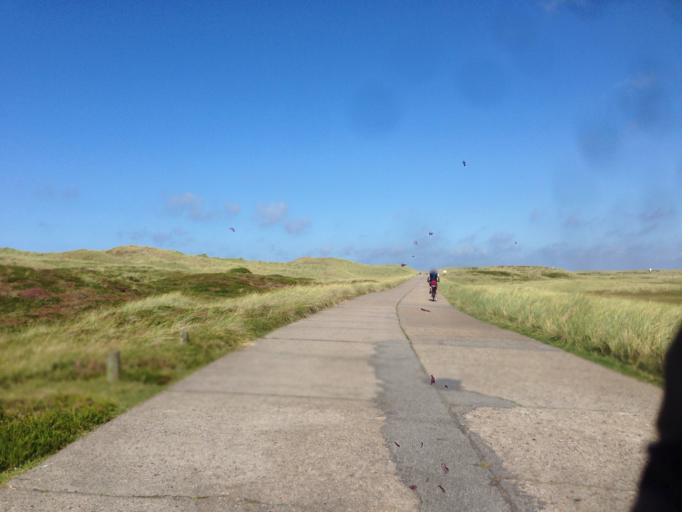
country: DE
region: Schleswig-Holstein
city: List
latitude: 55.0406
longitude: 8.3909
